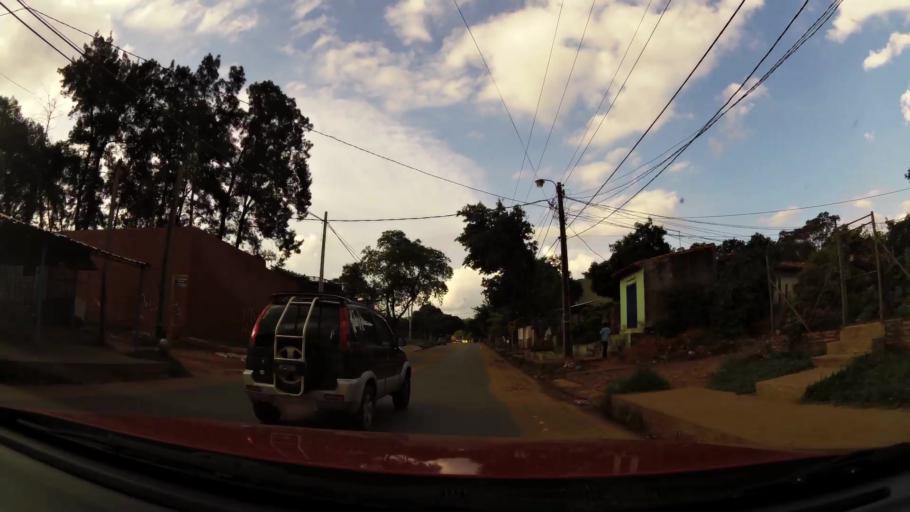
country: PY
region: Central
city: Nemby
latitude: -25.3682
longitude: -57.5411
